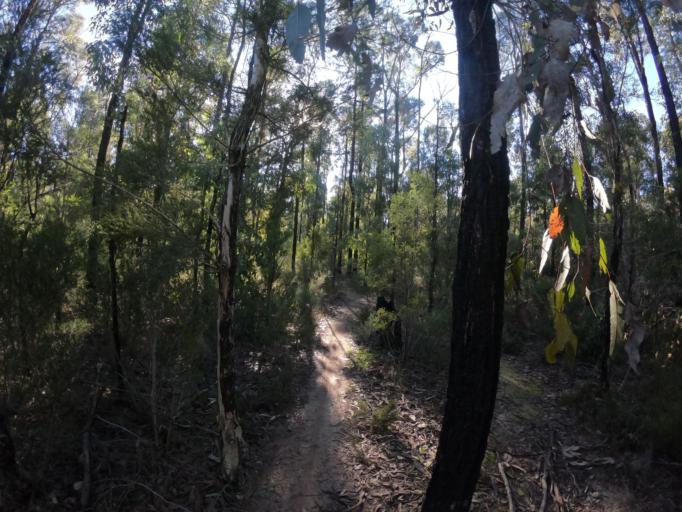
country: AU
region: New South Wales
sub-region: Hawkesbury
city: South Windsor
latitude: -33.6429
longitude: 150.7930
